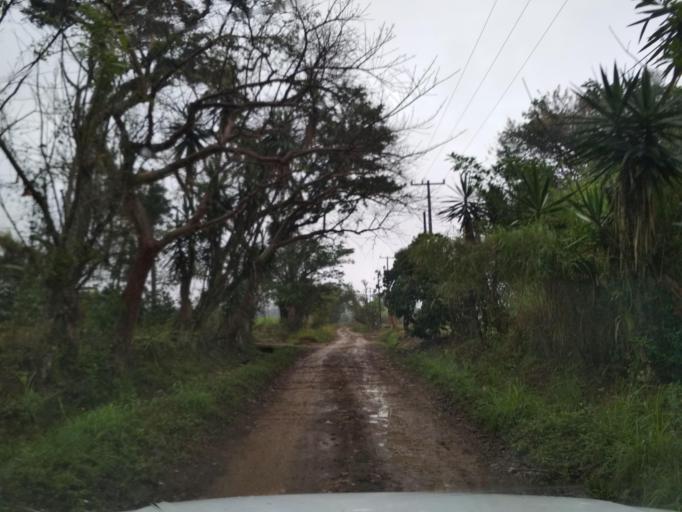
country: MX
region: Veracruz
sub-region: Amatlan de los Reyes
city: Centro de Readaptacion Social
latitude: 18.8244
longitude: -96.9381
